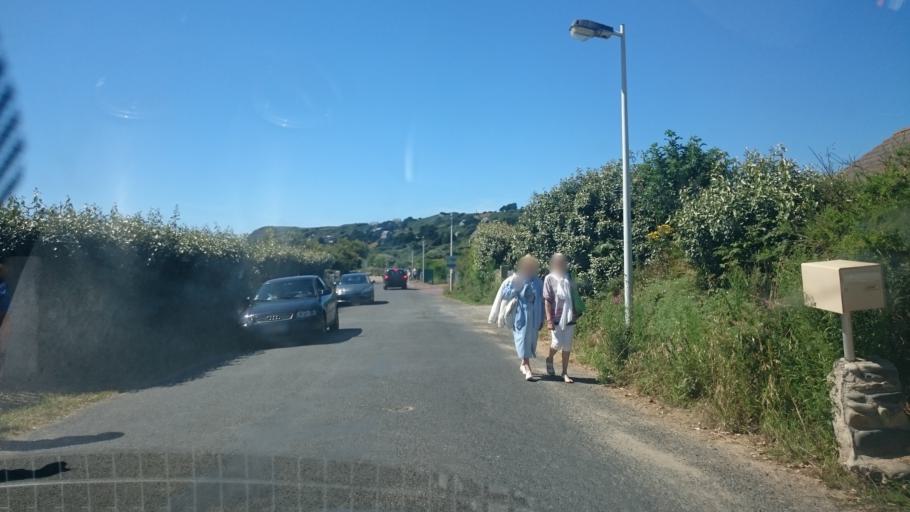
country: FR
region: Lower Normandy
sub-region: Departement de la Manche
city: Flamanville
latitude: 49.5080
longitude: -1.8482
